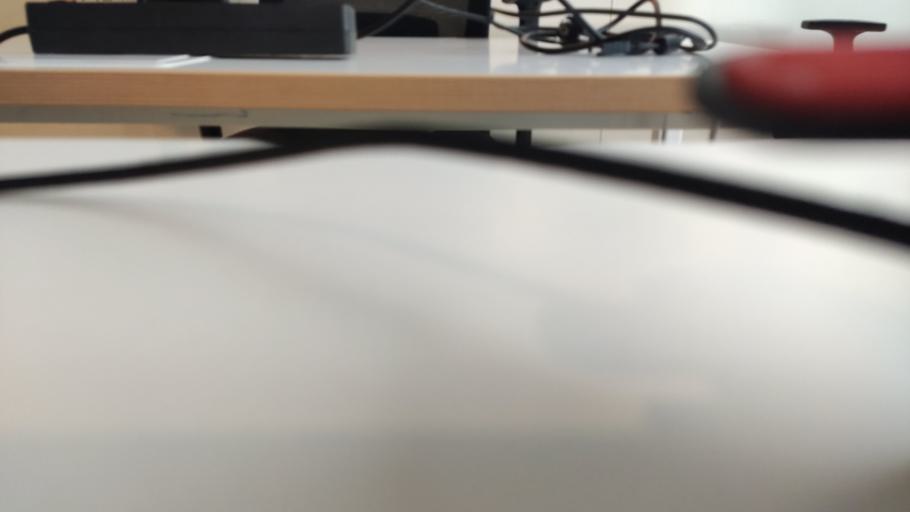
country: RU
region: Moskovskaya
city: Rogachevo
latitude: 56.4197
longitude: 37.0164
